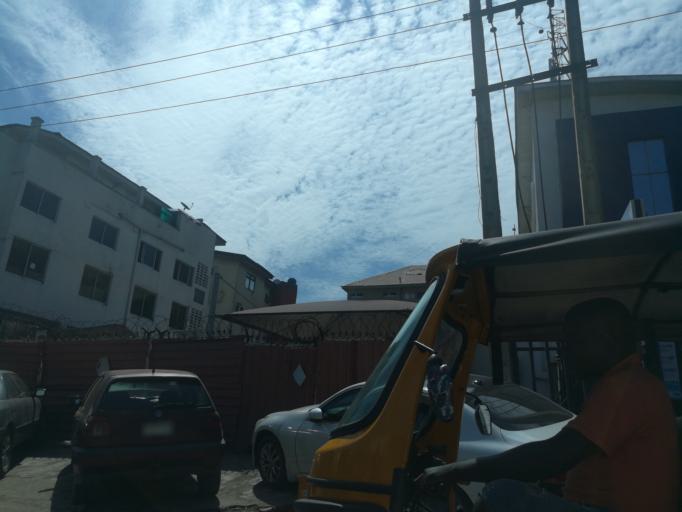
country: NG
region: Lagos
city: Ikeja
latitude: 6.6037
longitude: 3.3456
